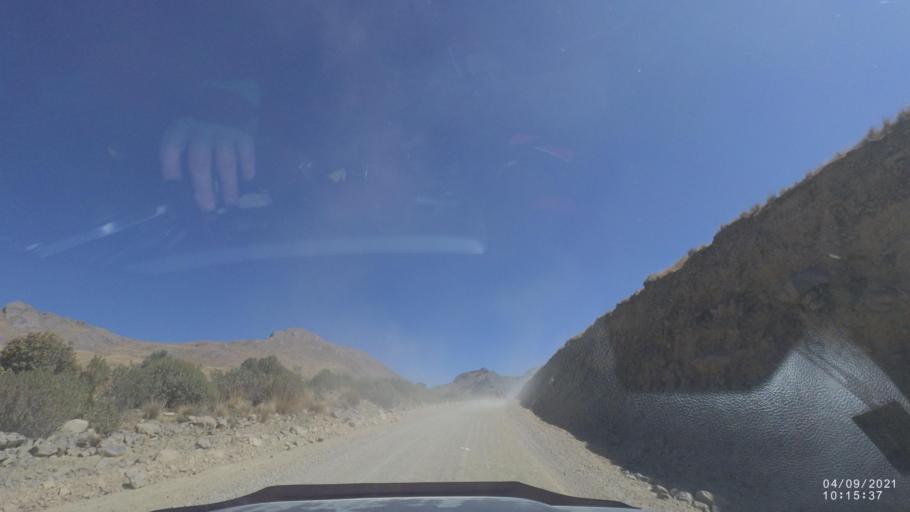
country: BO
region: Cochabamba
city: Sipe Sipe
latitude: -17.3258
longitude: -66.4159
